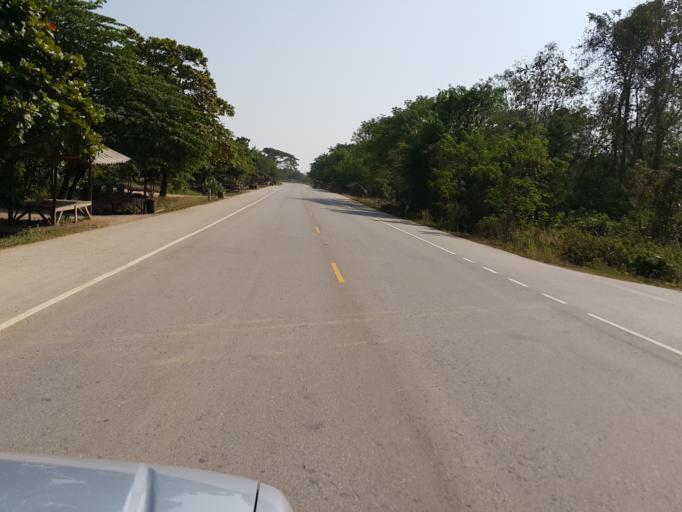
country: TH
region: Lampang
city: Mueang Pan
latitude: 18.8563
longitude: 99.5984
